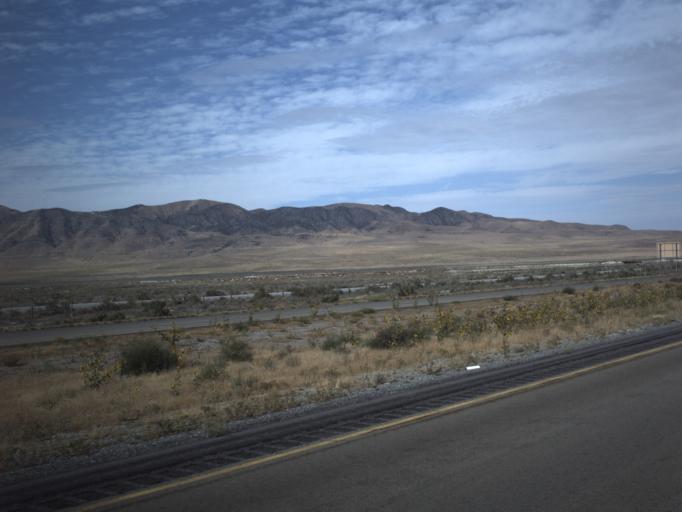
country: US
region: Utah
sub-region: Tooele County
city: Grantsville
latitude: 40.7695
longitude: -112.7933
